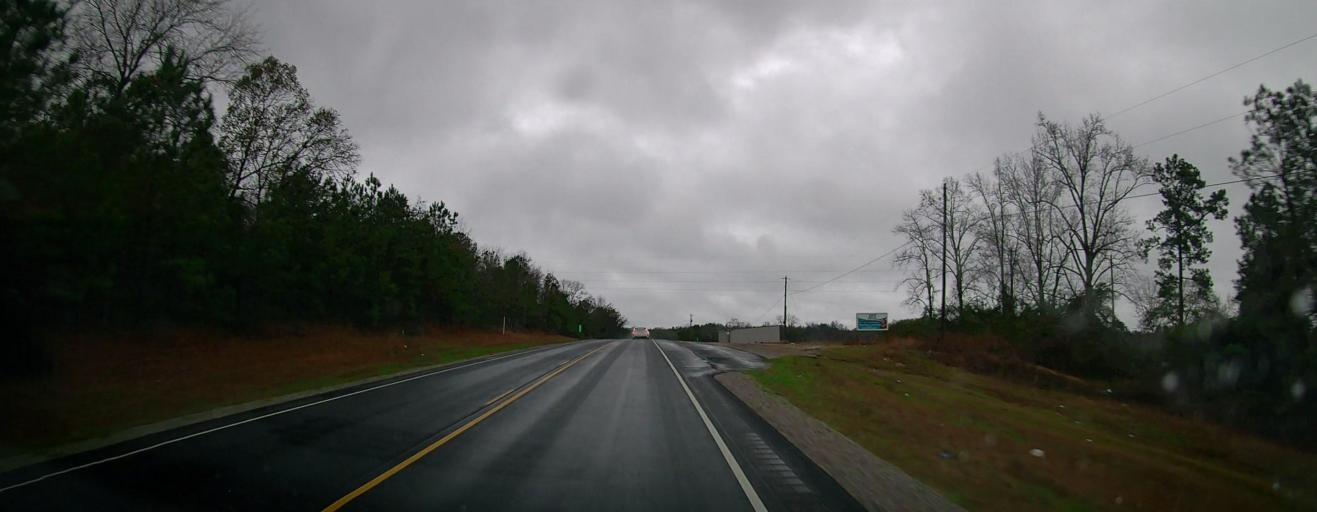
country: US
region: Alabama
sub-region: Chilton County
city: Clanton
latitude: 32.6437
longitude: -86.7584
